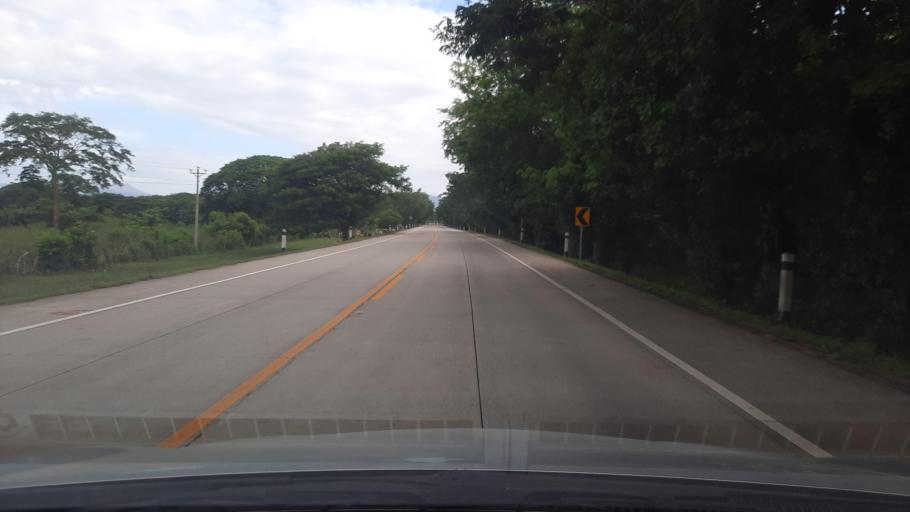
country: NI
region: Chinandega
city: Somotillo
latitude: 12.8275
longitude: -86.8973
